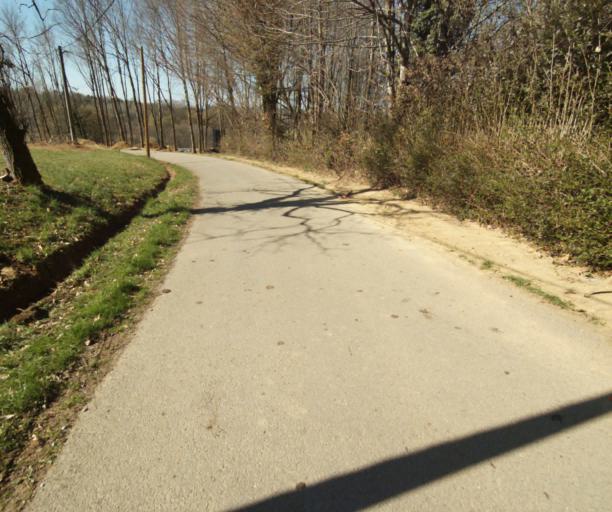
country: FR
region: Limousin
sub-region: Departement de la Correze
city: Saint-Clement
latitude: 45.3507
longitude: 1.6593
